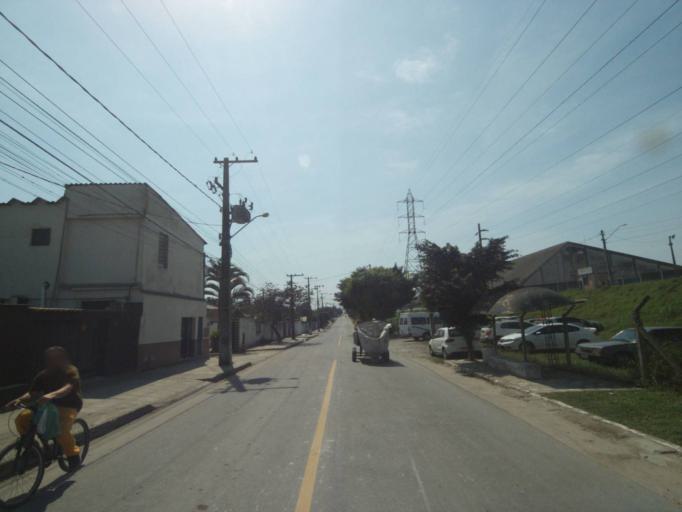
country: BR
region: Parana
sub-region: Paranagua
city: Paranagua
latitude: -25.5397
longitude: -48.5430
